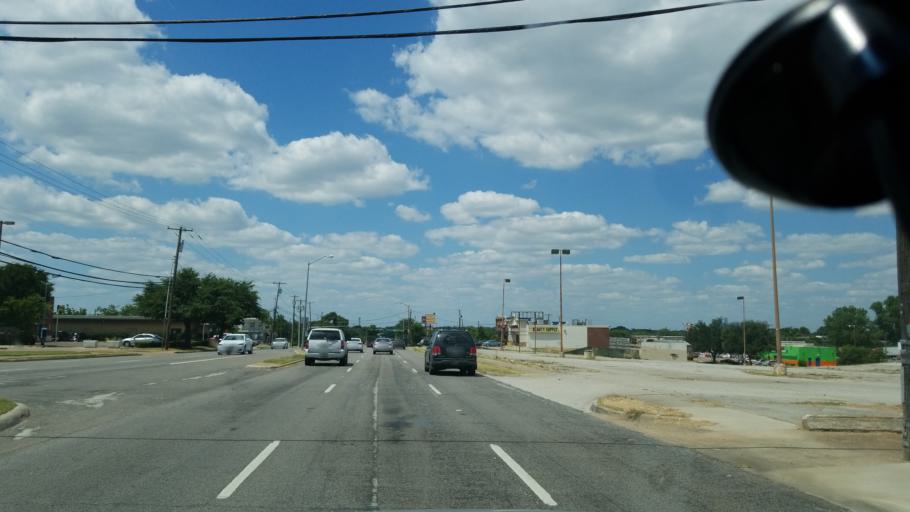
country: US
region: Texas
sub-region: Dallas County
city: Cockrell Hill
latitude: 32.6892
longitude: -96.8570
